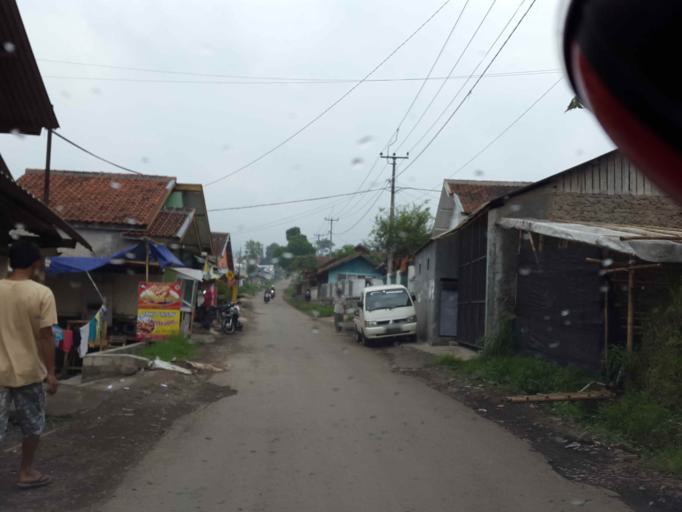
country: ID
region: West Java
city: Lembang
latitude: -6.8120
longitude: 107.5768
